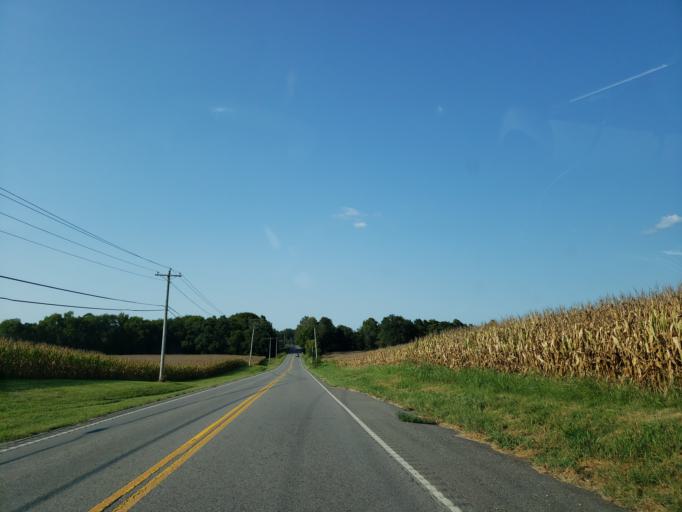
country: US
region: Tennessee
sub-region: Bradley County
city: Wildwood Lake
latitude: 35.0057
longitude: -84.7342
